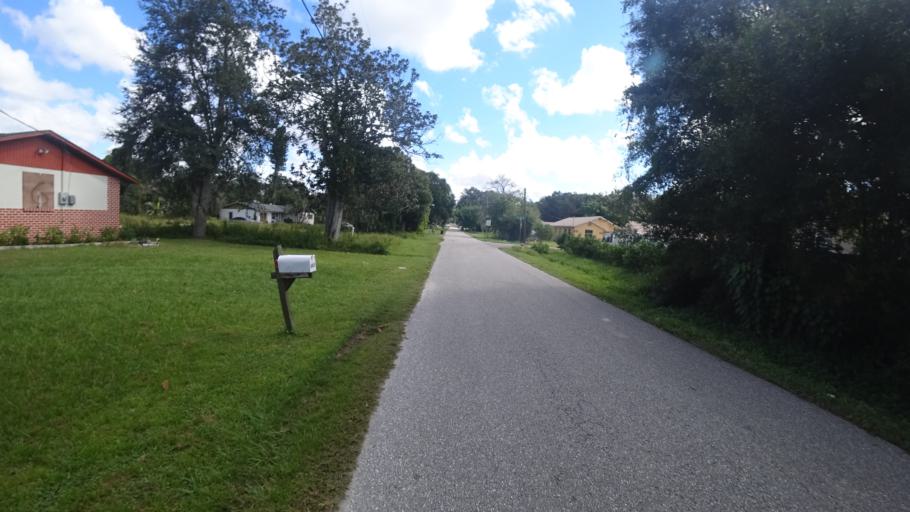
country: US
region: Florida
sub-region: Manatee County
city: West Samoset
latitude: 27.4752
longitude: -82.5572
